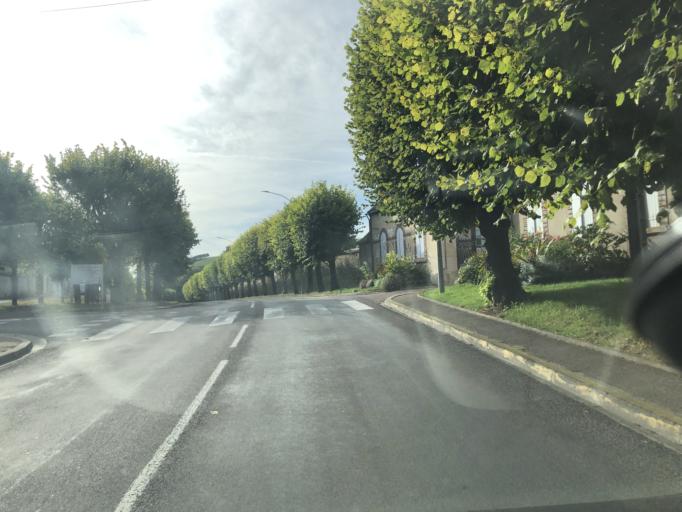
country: FR
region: Bourgogne
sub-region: Departement de l'Yonne
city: Joigny
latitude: 47.9845
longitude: 3.3990
